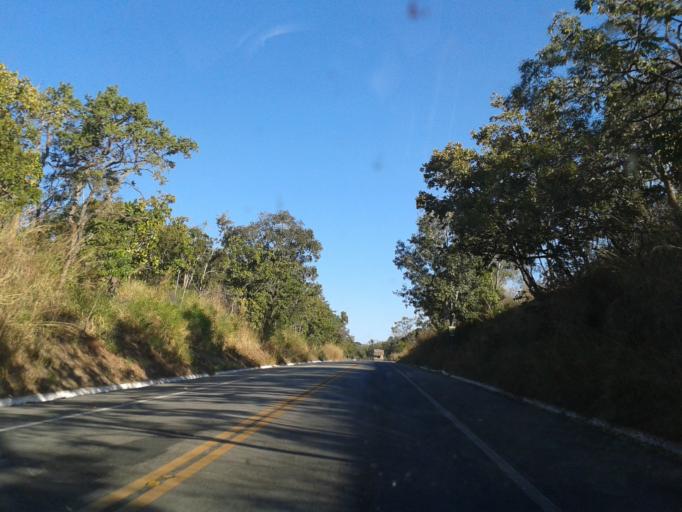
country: BR
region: Goias
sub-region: Itapuranga
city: Itapuranga
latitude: -15.5485
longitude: -50.2882
